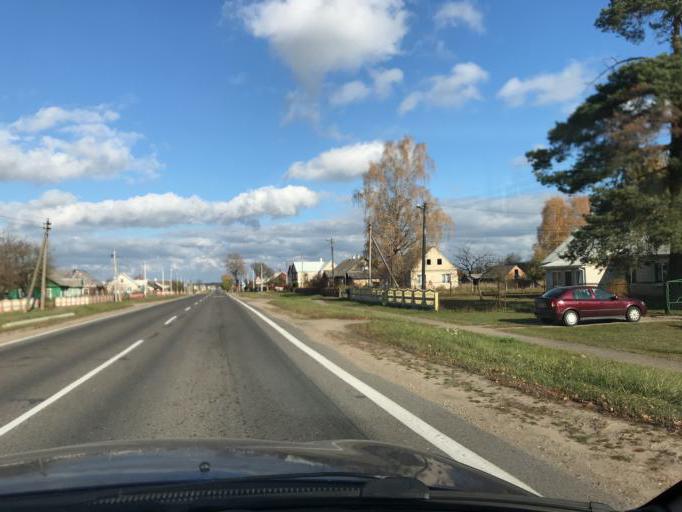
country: LT
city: Salcininkai
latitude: 54.2422
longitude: 25.3551
